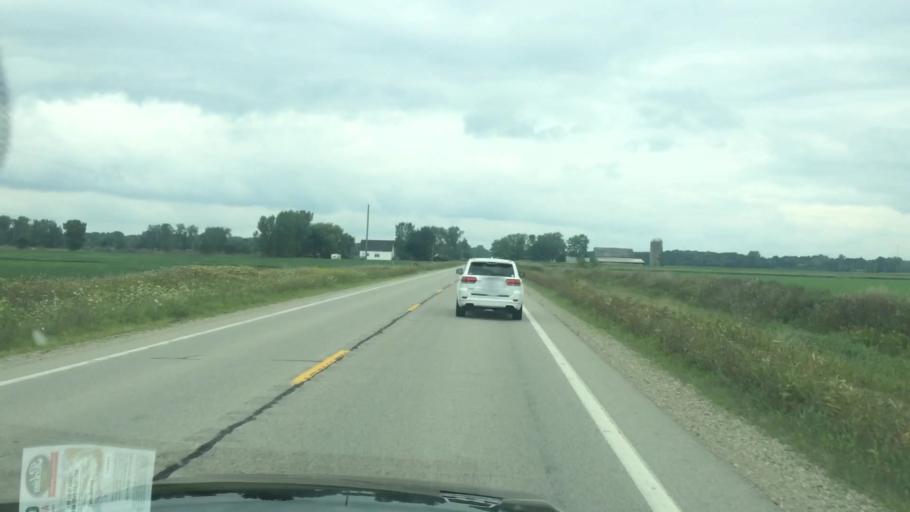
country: US
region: Michigan
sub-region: Sanilac County
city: Marlette
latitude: 43.4766
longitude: -83.0904
